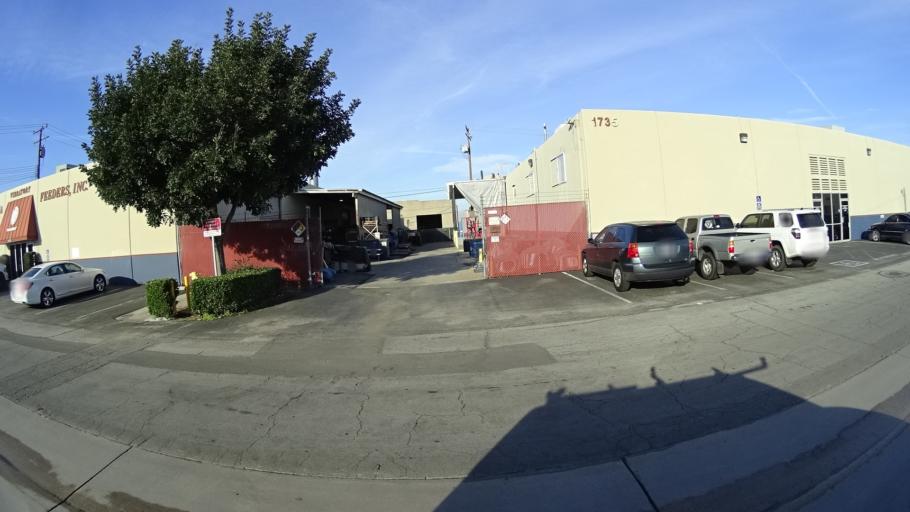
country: US
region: California
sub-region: Orange County
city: Fullerton
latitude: 33.8607
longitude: -117.9098
